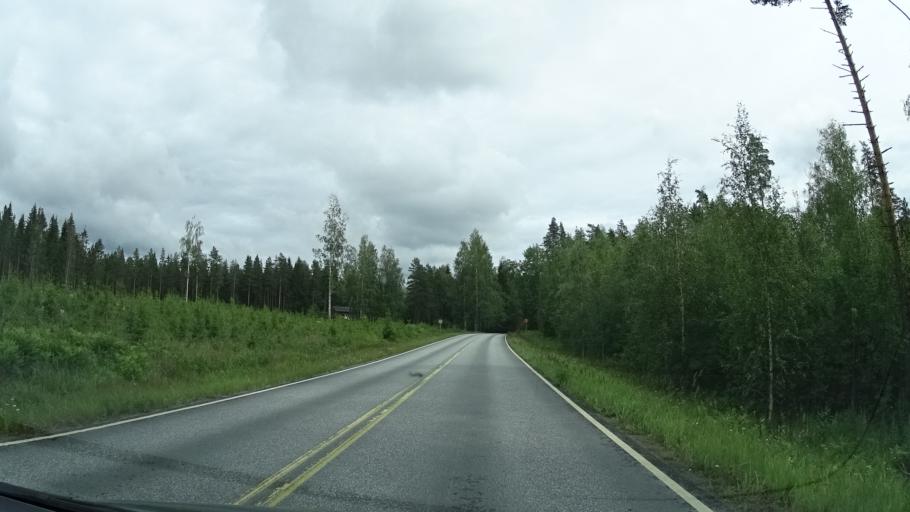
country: FI
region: Pirkanmaa
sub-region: Etelae-Pirkanmaa
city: Urjala
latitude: 61.0847
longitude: 23.4168
